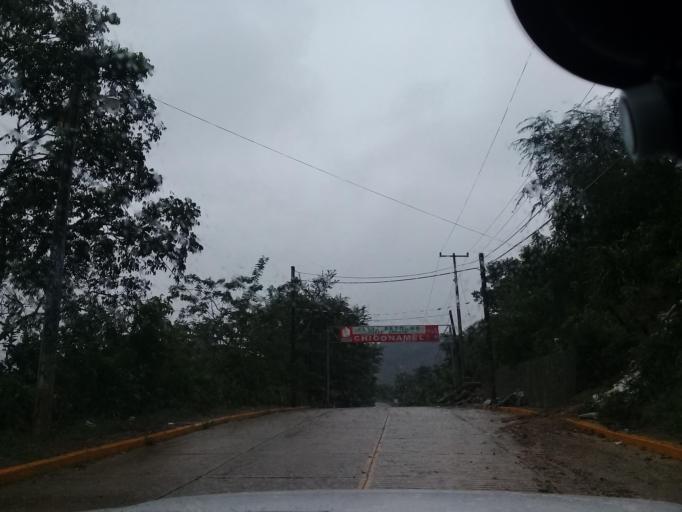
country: MX
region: Veracruz
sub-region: Chalma
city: San Pedro Coyutla
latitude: 21.2317
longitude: -98.4550
